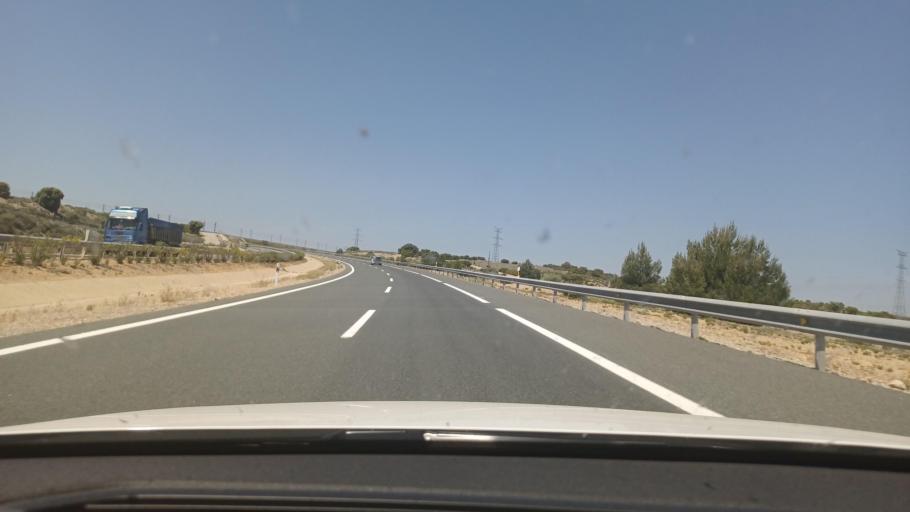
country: ES
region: Castille-La Mancha
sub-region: Provincia de Albacete
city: Alpera
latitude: 38.8807
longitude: -1.2488
